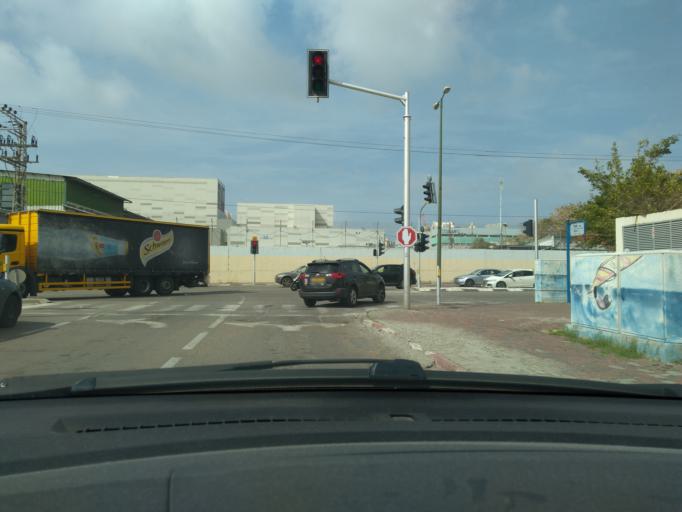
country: IL
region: Central District
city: Even Yehuda
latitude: 32.2749
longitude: 34.8599
